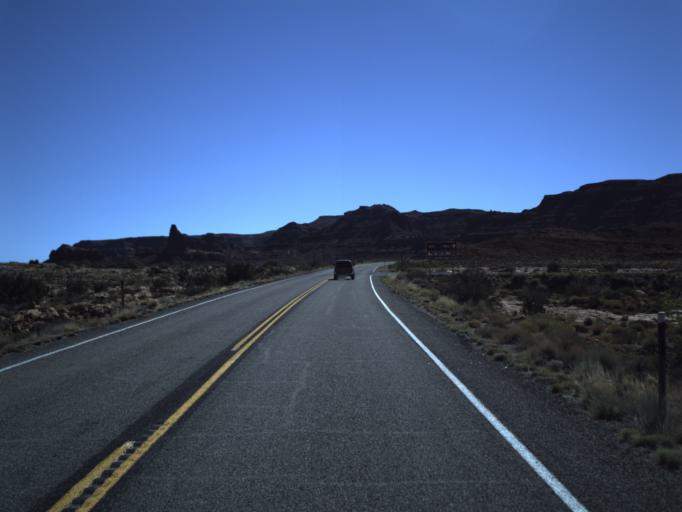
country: US
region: Utah
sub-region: San Juan County
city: Blanding
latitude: 37.8809
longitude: -110.3559
